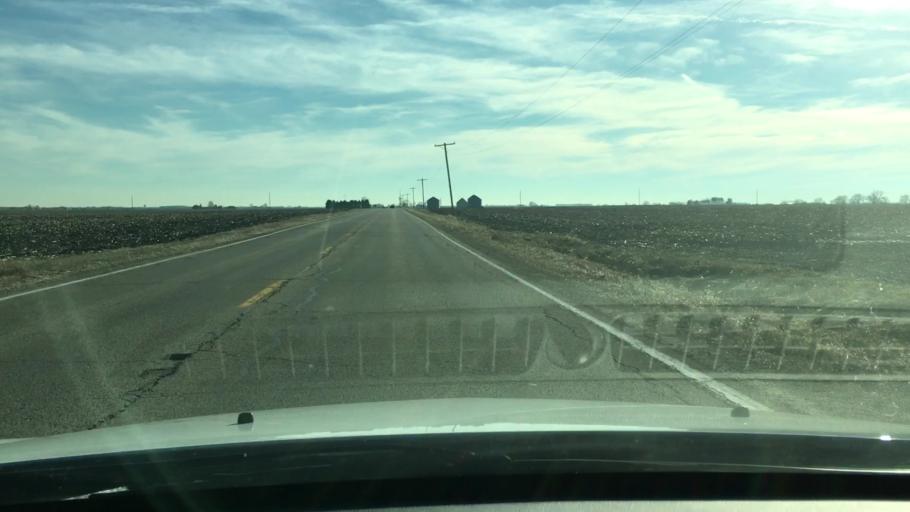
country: US
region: Illinois
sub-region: LaSalle County
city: Mendota
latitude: 41.4475
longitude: -89.1268
